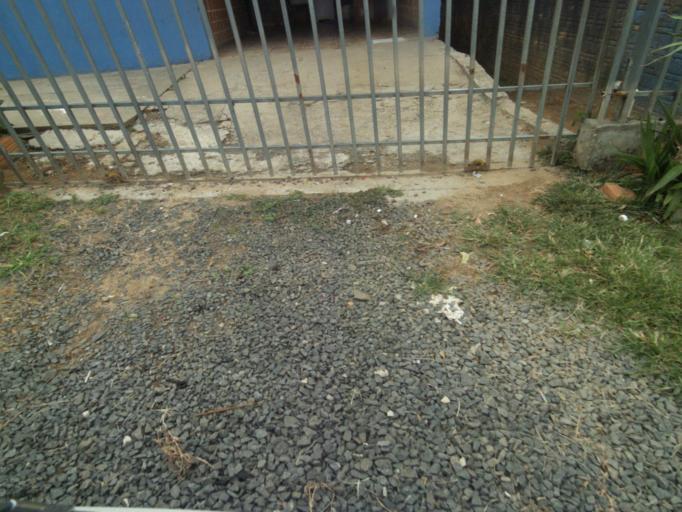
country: BR
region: Parana
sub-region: Palmeira
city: Palmeira
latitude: -25.4351
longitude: -50.0054
